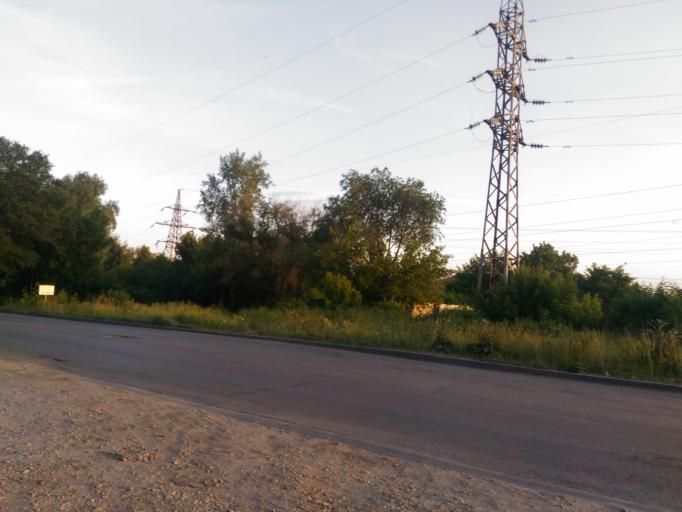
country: RU
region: Ulyanovsk
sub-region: Ulyanovskiy Rayon
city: Ulyanovsk
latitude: 54.3349
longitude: 48.3644
